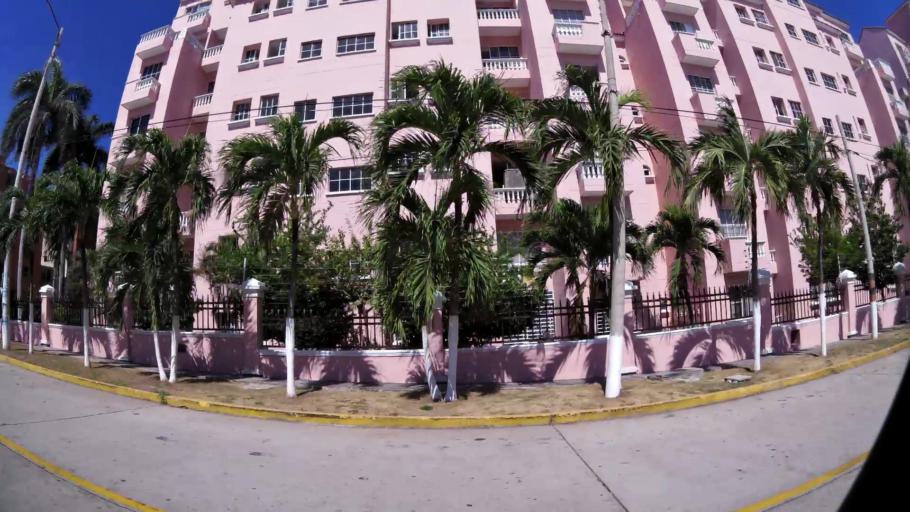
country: CO
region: Atlantico
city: Barranquilla
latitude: 11.0118
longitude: -74.8207
